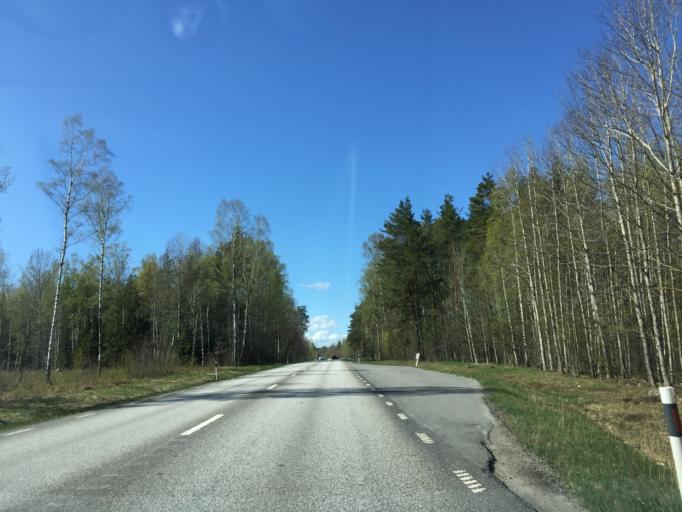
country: SE
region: OErebro
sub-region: Hallsbergs Kommun
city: Skollersta
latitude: 59.1330
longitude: 15.2882
